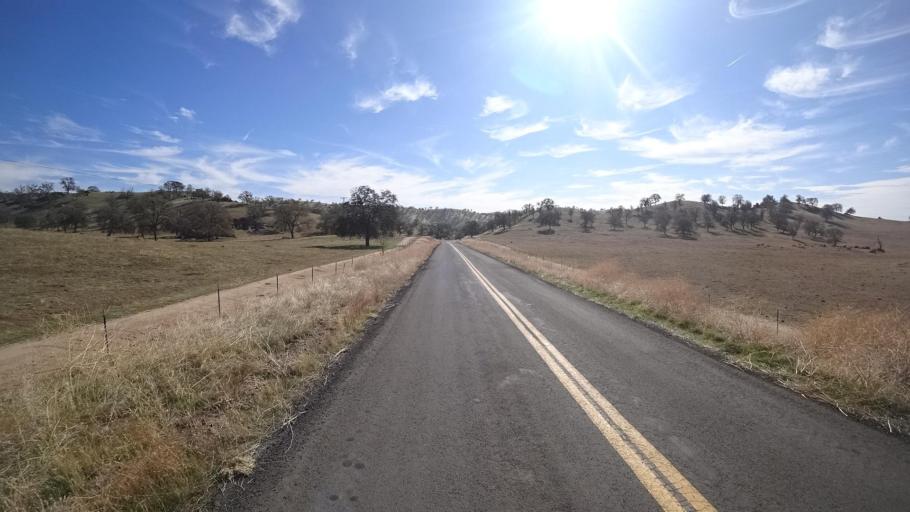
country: US
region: California
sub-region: Kern County
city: Oildale
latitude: 35.6426
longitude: -118.8382
